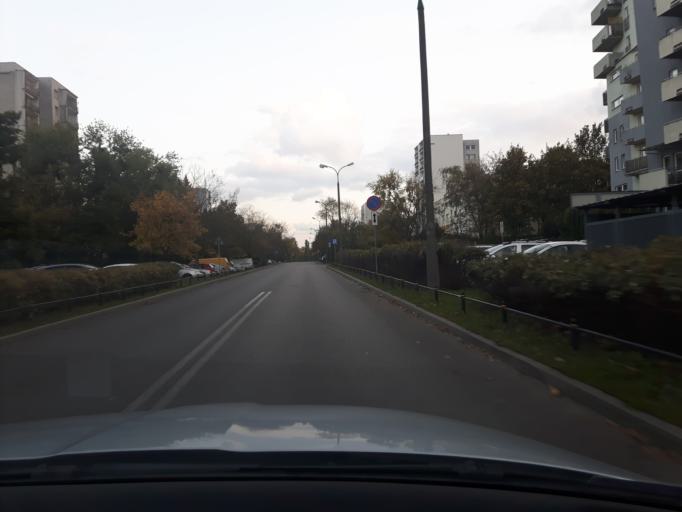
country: PL
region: Masovian Voivodeship
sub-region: Warszawa
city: Ursynow
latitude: 52.1428
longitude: 21.0498
